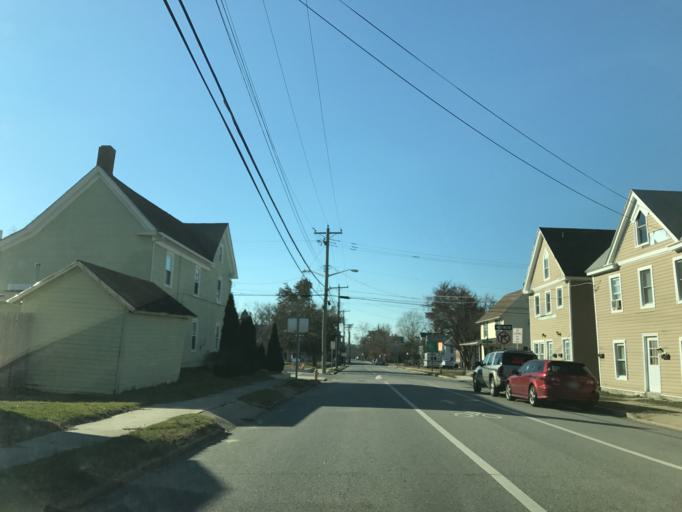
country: US
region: Maryland
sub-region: Caroline County
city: Denton
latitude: 38.8866
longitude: -75.8296
